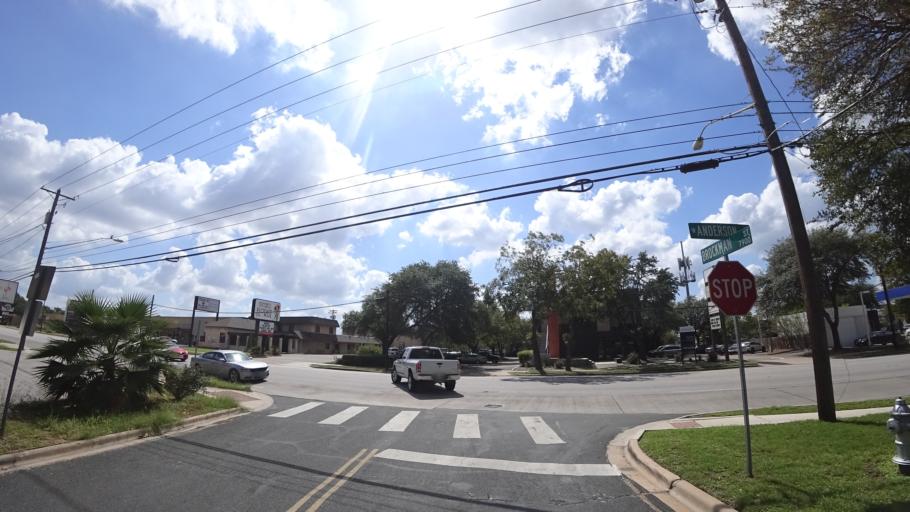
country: US
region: Texas
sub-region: Travis County
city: Austin
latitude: 30.3559
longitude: -97.7299
